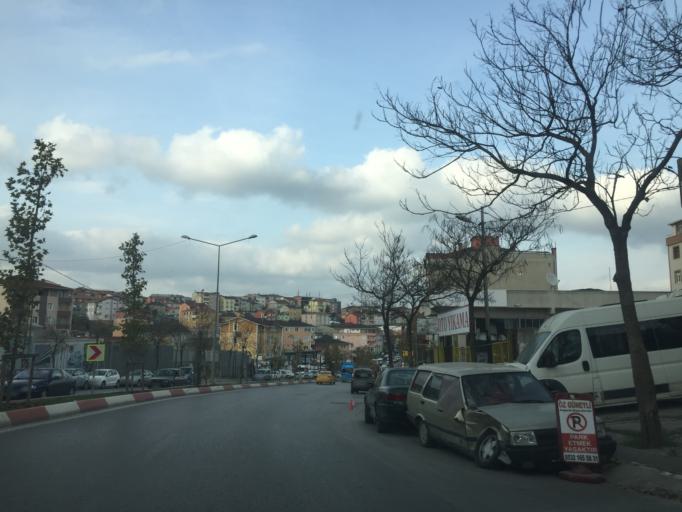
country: TR
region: Istanbul
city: Sultanbeyli
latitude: 40.9456
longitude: 29.2993
